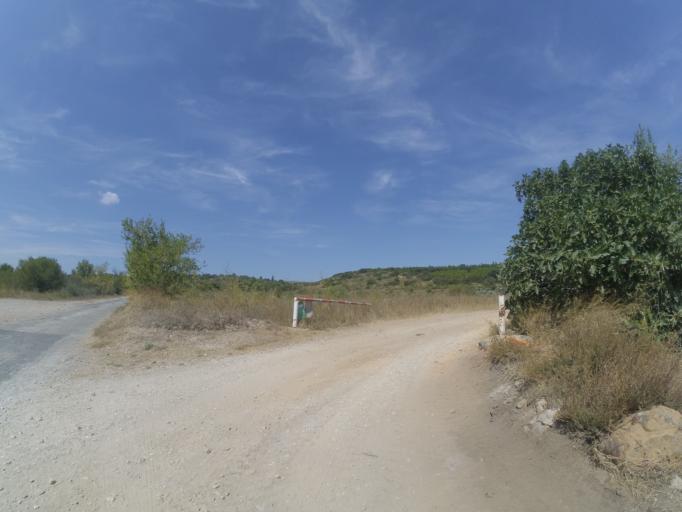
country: FR
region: Languedoc-Roussillon
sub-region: Departement des Pyrenees-Orientales
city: Baixas
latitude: 42.7498
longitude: 2.7994
